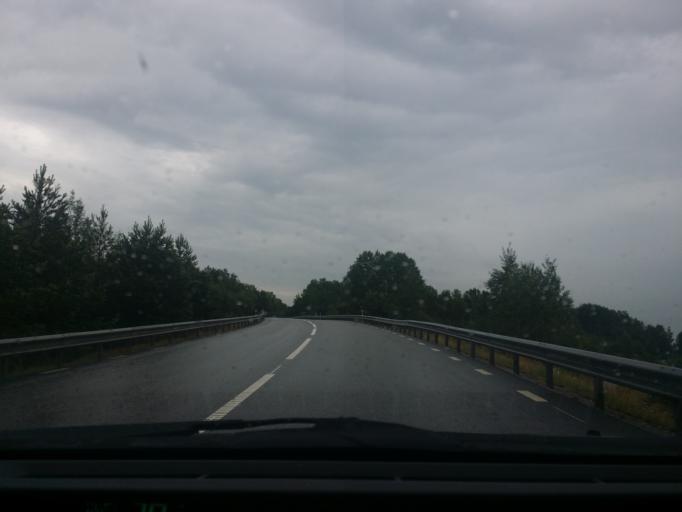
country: SE
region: OErebro
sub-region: Lindesbergs Kommun
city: Fellingsbro
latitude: 59.4171
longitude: 15.6851
